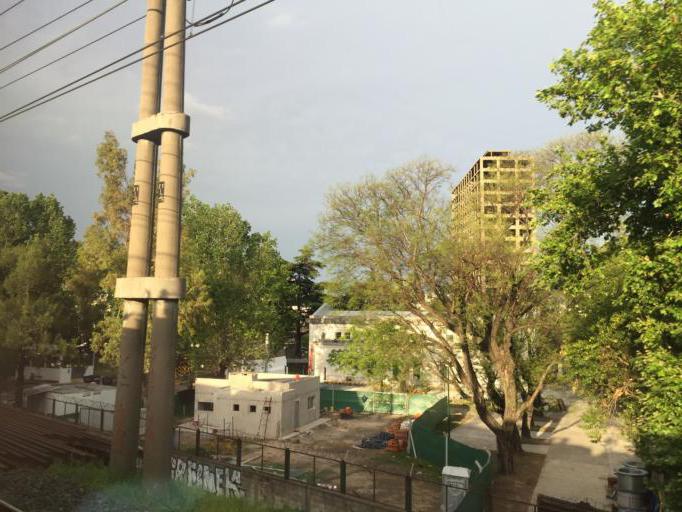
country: AR
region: Buenos Aires
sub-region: Partido de Avellaneda
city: Avellaneda
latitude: -34.6435
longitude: -58.3808
